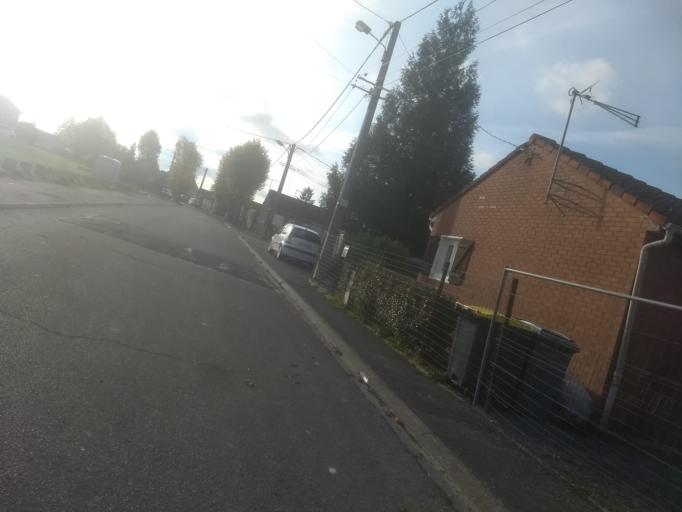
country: FR
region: Nord-Pas-de-Calais
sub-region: Departement du Pas-de-Calais
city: Arras
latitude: 50.2797
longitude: 2.7771
